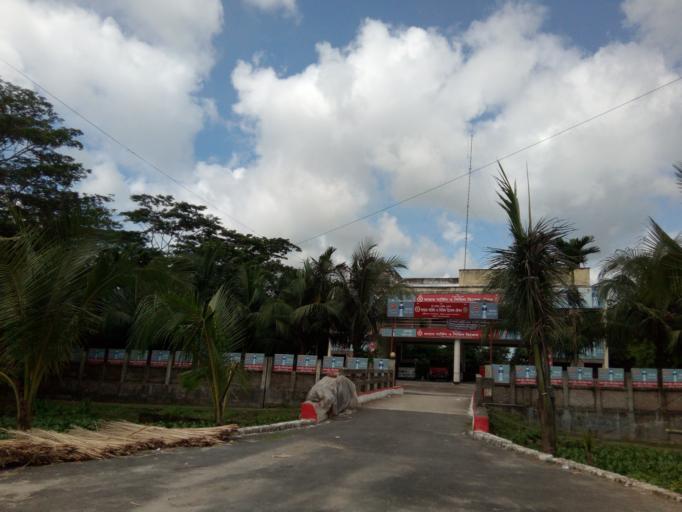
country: BD
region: Dhaka
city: Tungipara
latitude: 22.8966
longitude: 89.8892
